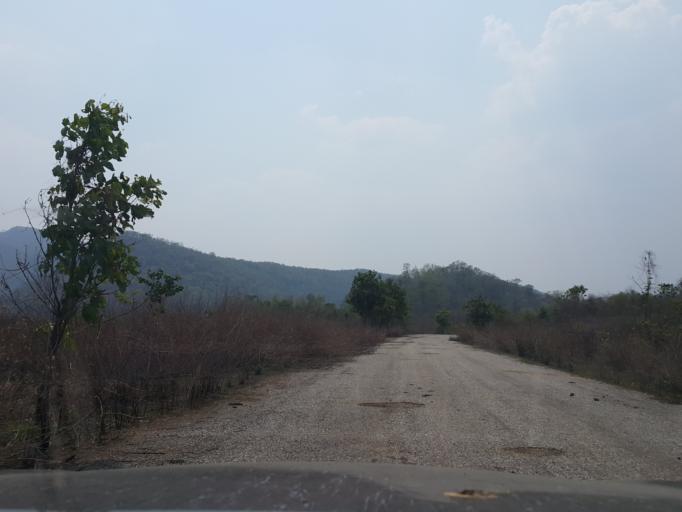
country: TH
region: Lampang
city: Mae Phrik
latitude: 17.5012
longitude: 99.0364
